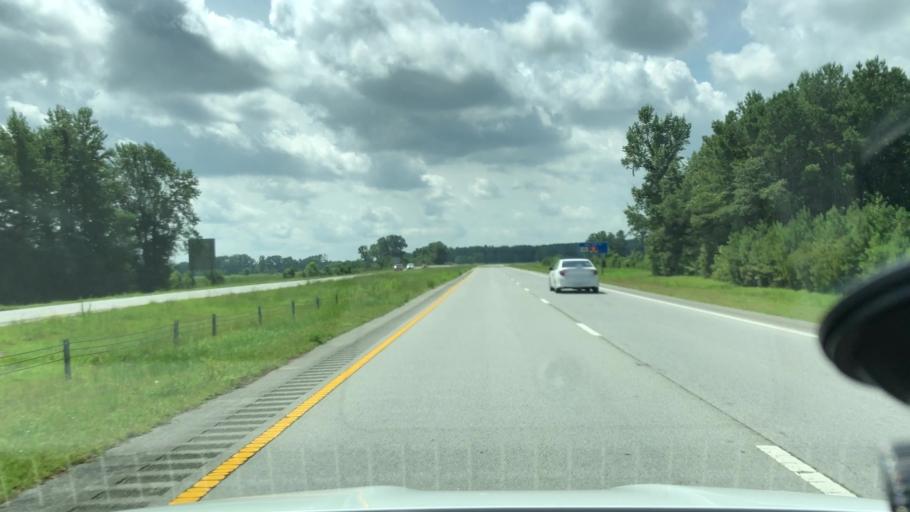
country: US
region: North Carolina
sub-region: Beaufort County
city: Washington
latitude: 35.5146
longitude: -77.0864
